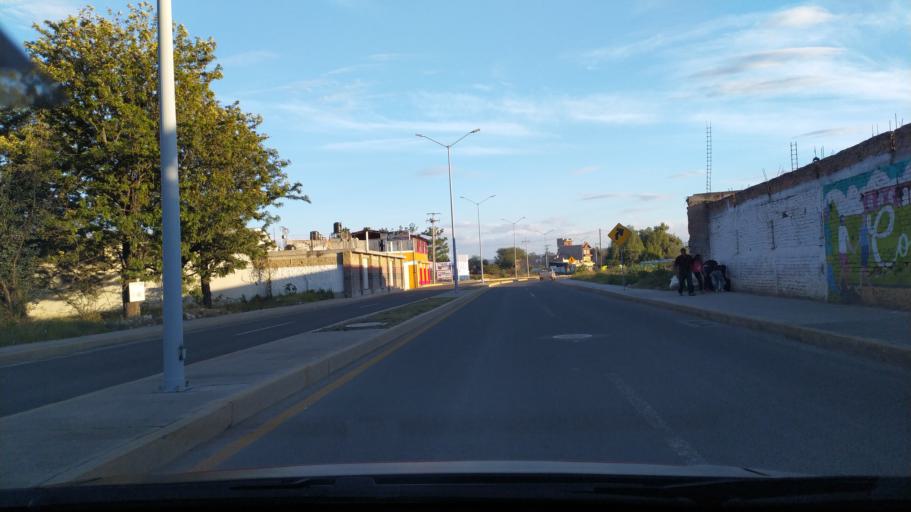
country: MX
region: Guanajuato
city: Ciudad Manuel Doblado
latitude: 20.7334
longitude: -101.9470
